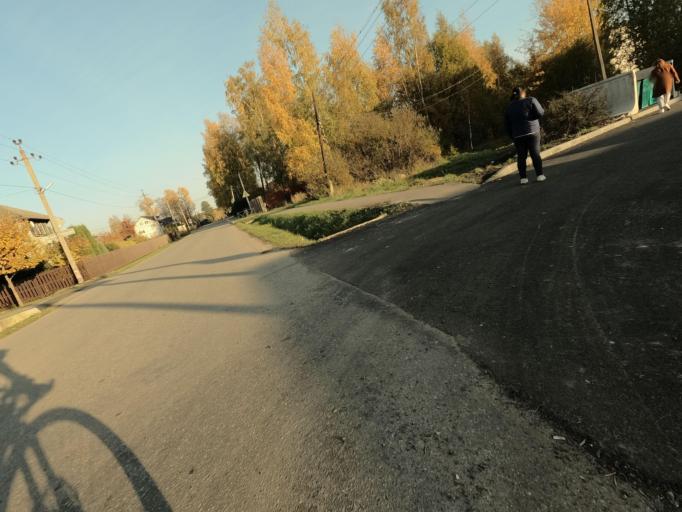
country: RU
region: Leningrad
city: Mga
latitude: 59.7607
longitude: 31.0677
